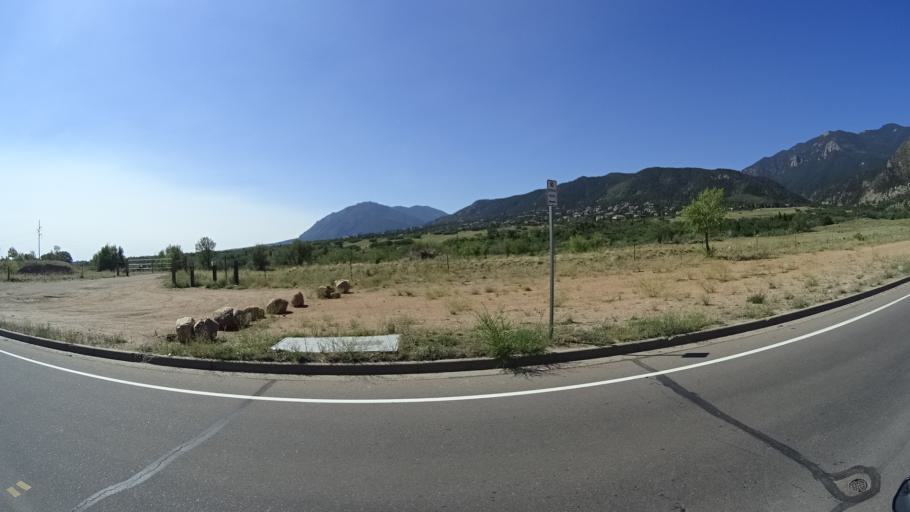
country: US
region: Colorado
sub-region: El Paso County
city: Colorado Springs
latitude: 38.8308
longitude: -104.8711
